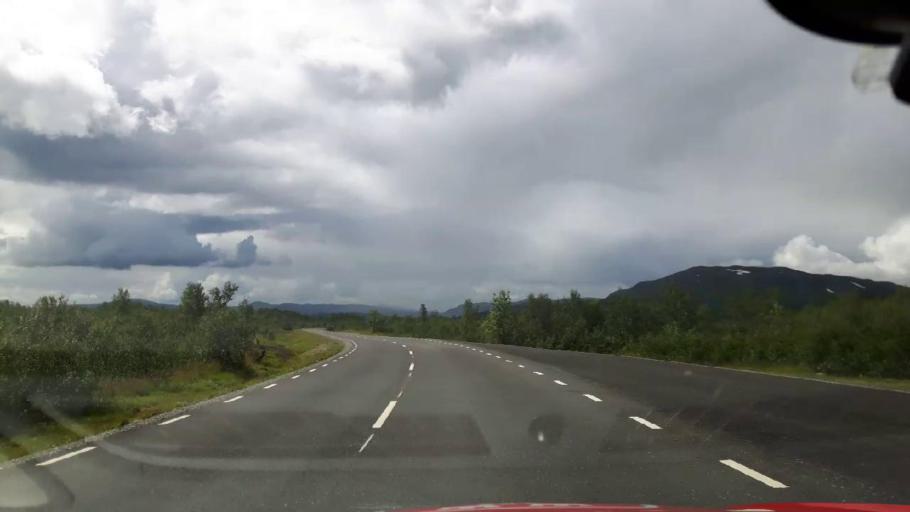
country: NO
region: Nordland
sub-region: Hattfjelldal
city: Hattfjelldal
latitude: 64.9999
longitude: 14.2426
